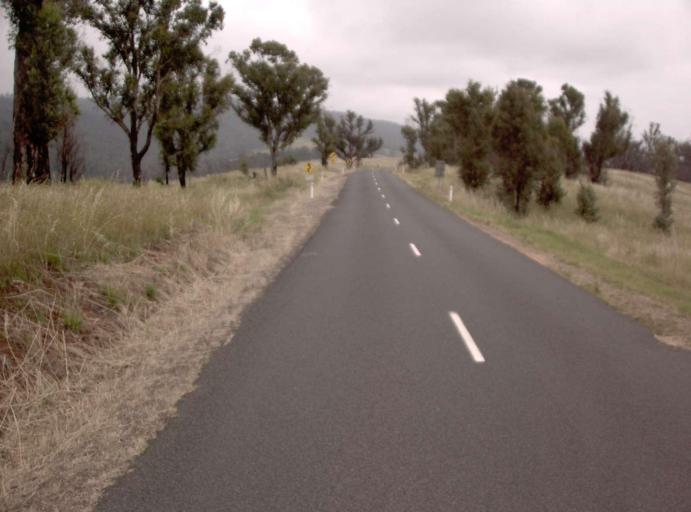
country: AU
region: Victoria
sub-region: Wellington
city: Heyfield
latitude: -37.8321
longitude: 146.6785
